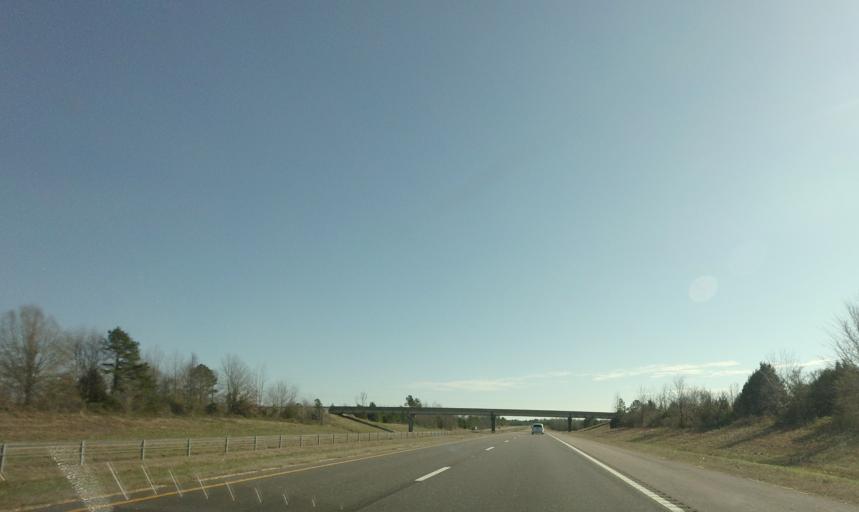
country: US
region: Mississippi
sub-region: Union County
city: New Albany
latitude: 34.5301
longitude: -89.0833
